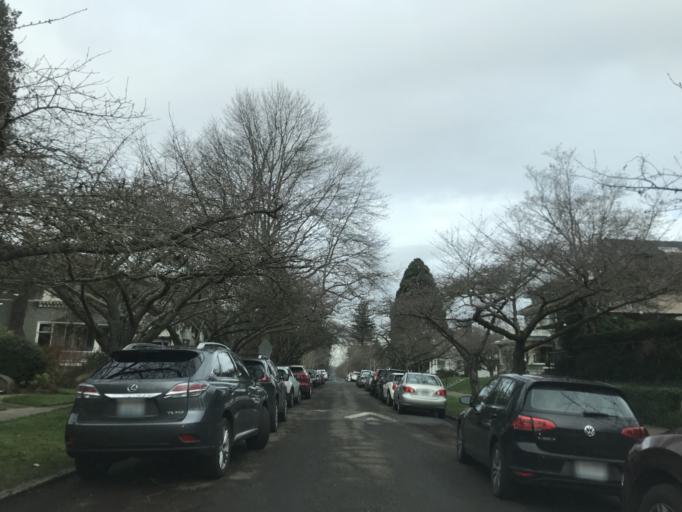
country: US
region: Washington
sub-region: King County
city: Seattle
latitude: 47.6279
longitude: -122.3048
